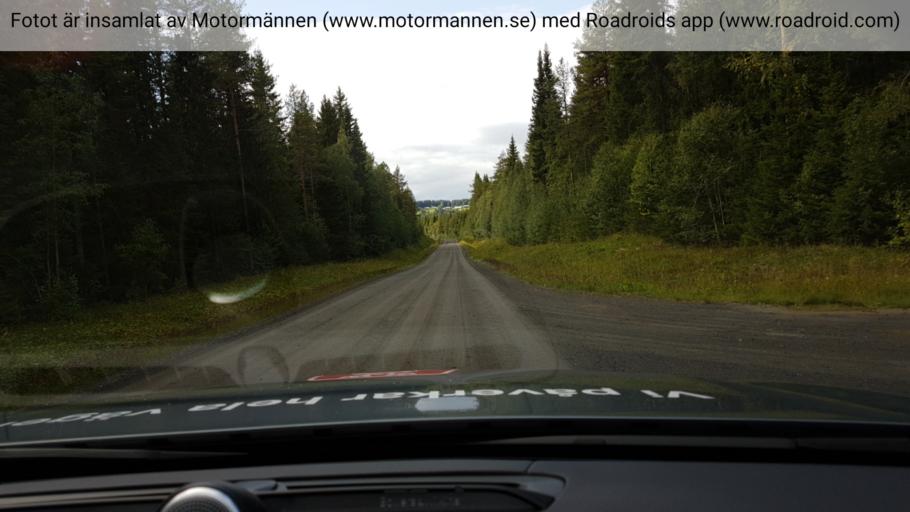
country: SE
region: Jaemtland
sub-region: OEstersunds Kommun
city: Lit
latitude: 63.6795
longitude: 14.7686
